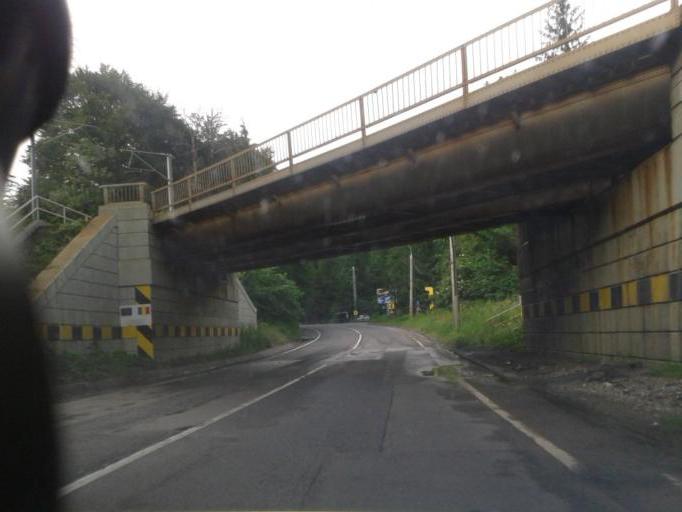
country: RO
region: Prahova
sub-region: Oras Azuga
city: Azuga
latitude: 45.4284
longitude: 25.5532
